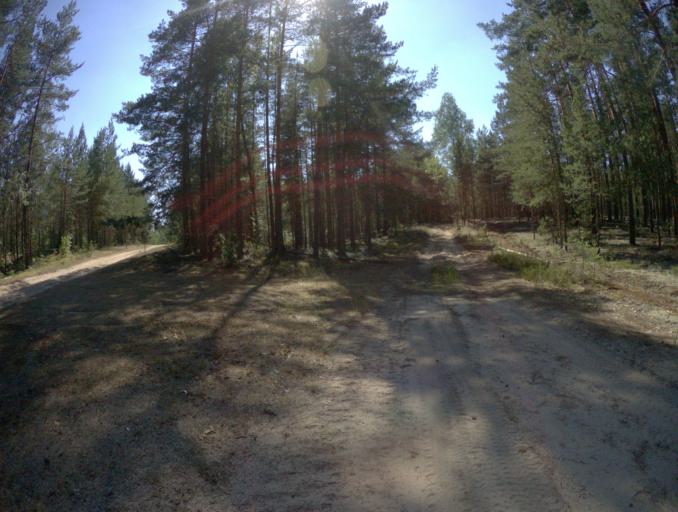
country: RU
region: Ivanovo
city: Talitsy
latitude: 56.3903
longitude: 42.2545
